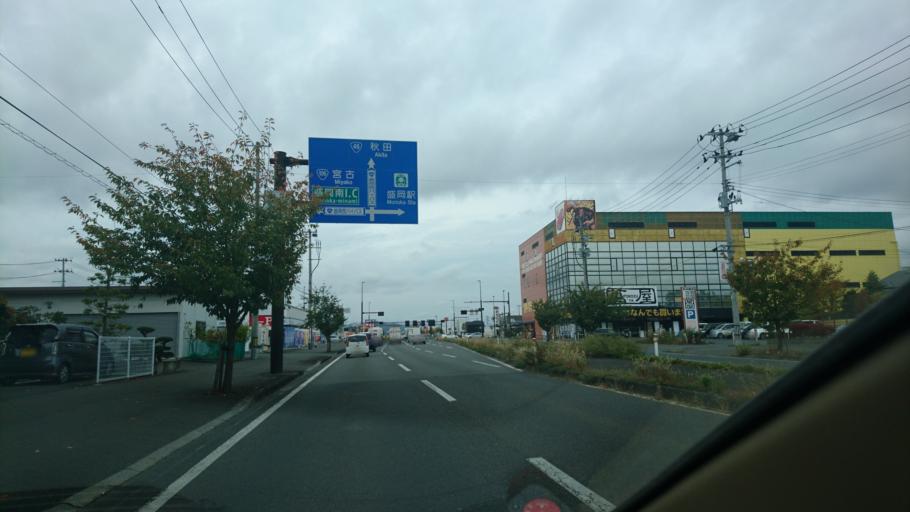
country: JP
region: Iwate
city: Morioka-shi
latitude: 39.6847
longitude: 141.1373
